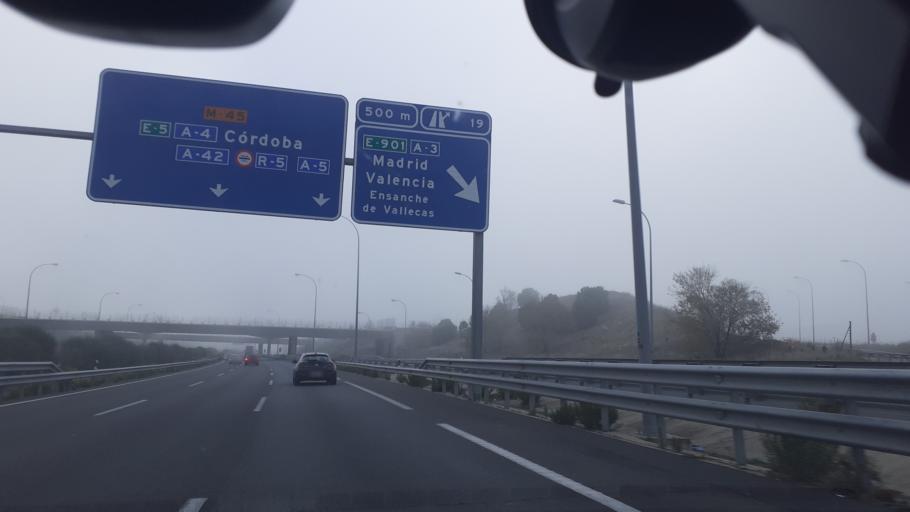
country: ES
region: Madrid
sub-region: Provincia de Madrid
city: Vicalvaro
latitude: 40.3882
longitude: -3.5848
